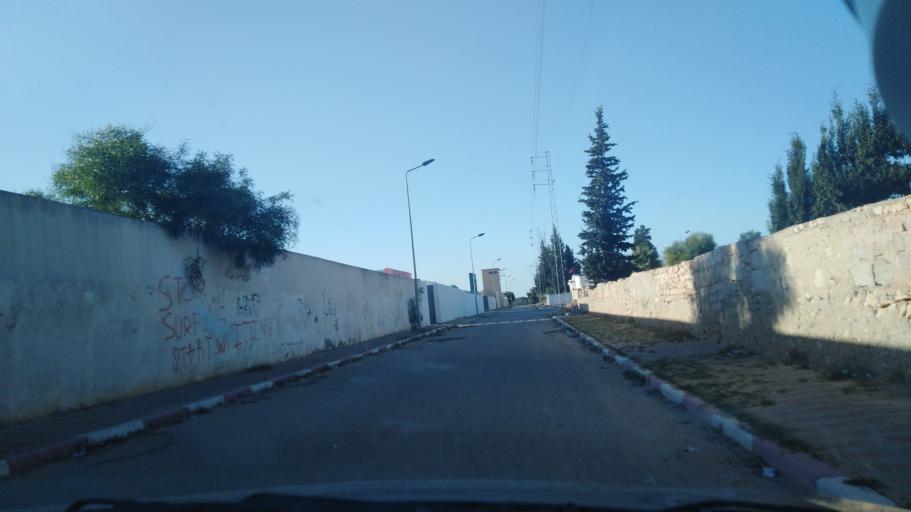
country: TN
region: Al Mahdiyah
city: Shurban
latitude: 34.9646
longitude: 10.3695
